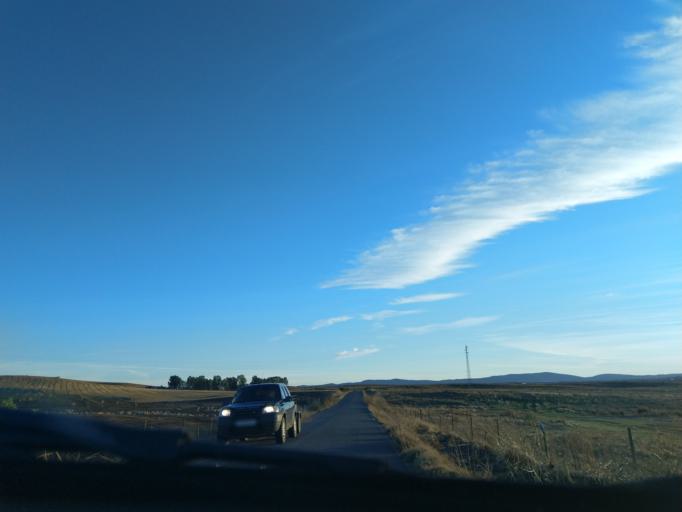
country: ES
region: Extremadura
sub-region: Provincia de Badajoz
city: Berlanga
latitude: 38.2611
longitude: -5.8260
